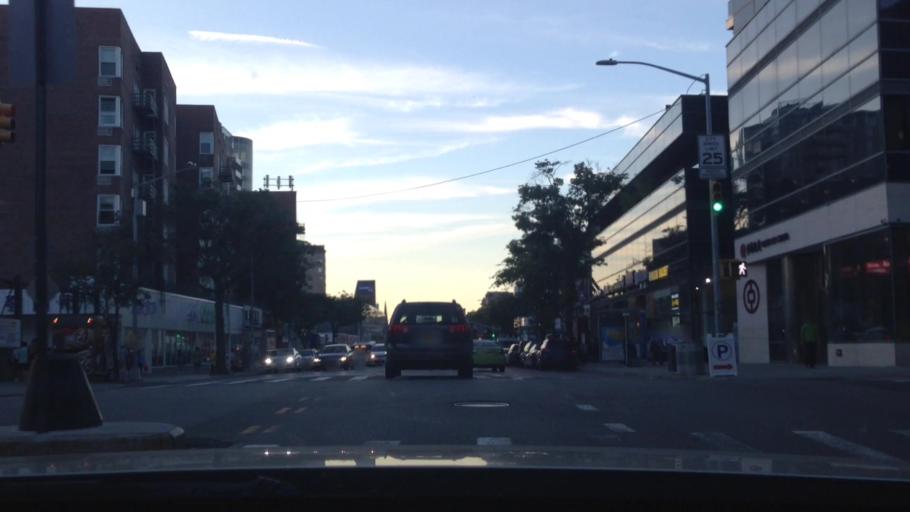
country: US
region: New York
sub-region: Queens County
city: Jamaica
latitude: 40.7542
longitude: -73.8278
